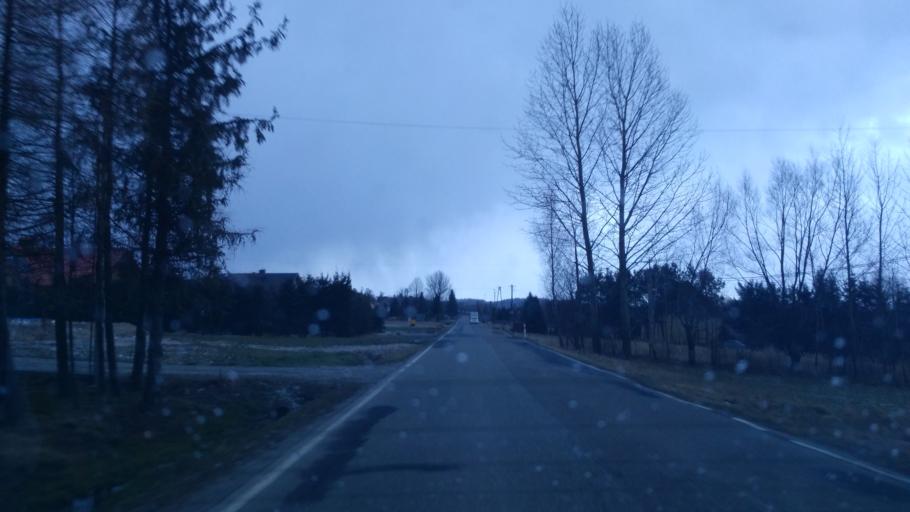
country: PL
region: Subcarpathian Voivodeship
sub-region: Powiat rzeszowski
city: Hyzne
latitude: 49.9269
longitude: 22.1916
